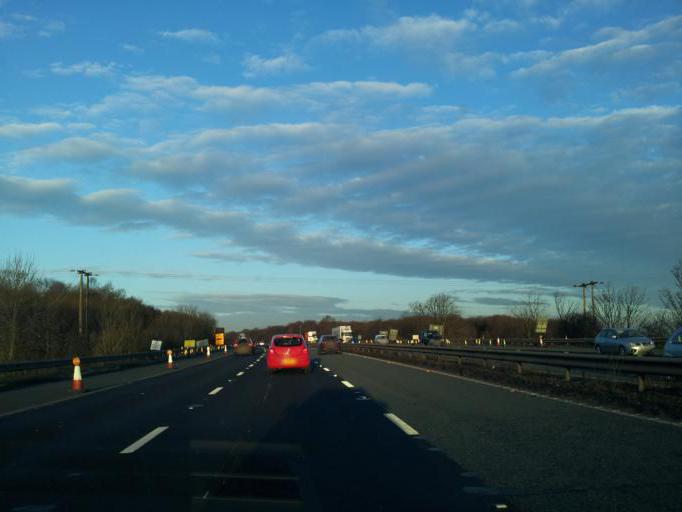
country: GB
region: England
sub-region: City and Borough of Wakefield
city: Castleford
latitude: 53.7072
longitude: -1.3686
